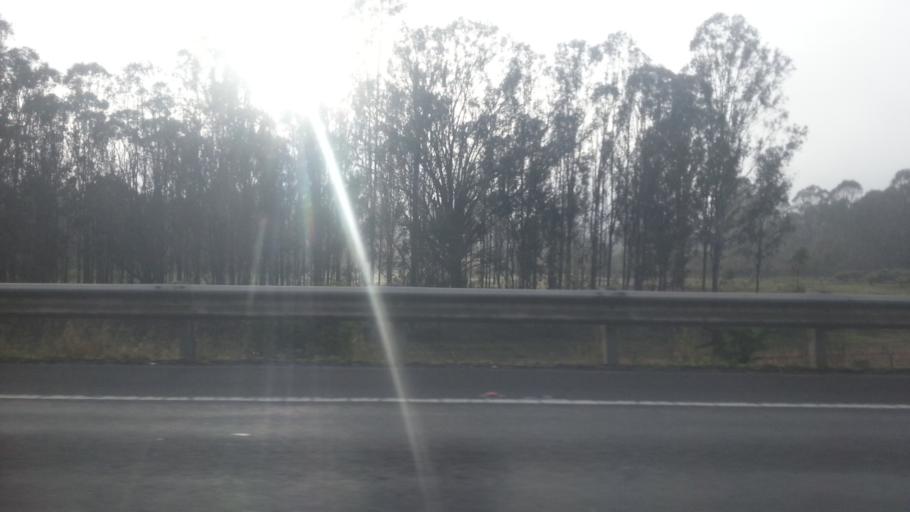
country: AU
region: New South Wales
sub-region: Penrith Municipality
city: Mulgoa
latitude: -33.8270
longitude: 150.6834
